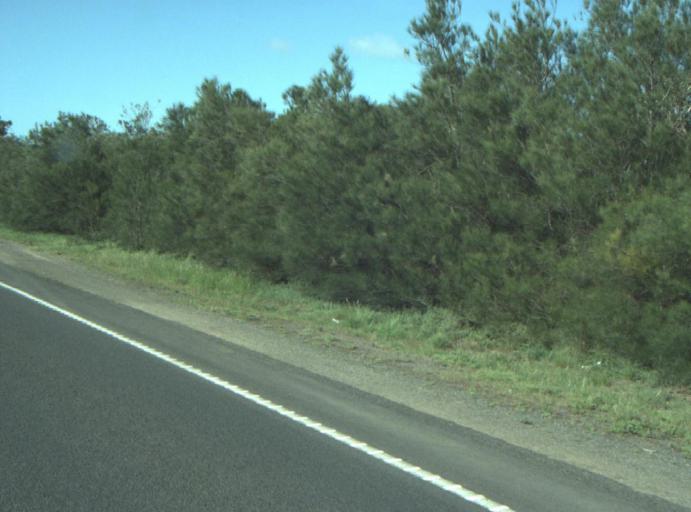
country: AU
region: Victoria
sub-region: Greater Geelong
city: Lara
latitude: -38.0119
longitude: 144.3509
